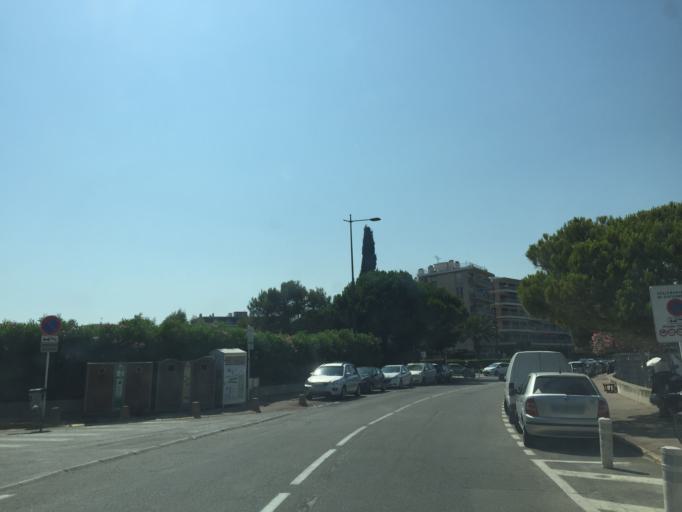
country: FR
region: Provence-Alpes-Cote d'Azur
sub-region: Departement des Alpes-Maritimes
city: Antibes
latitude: 43.5689
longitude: 7.1313
